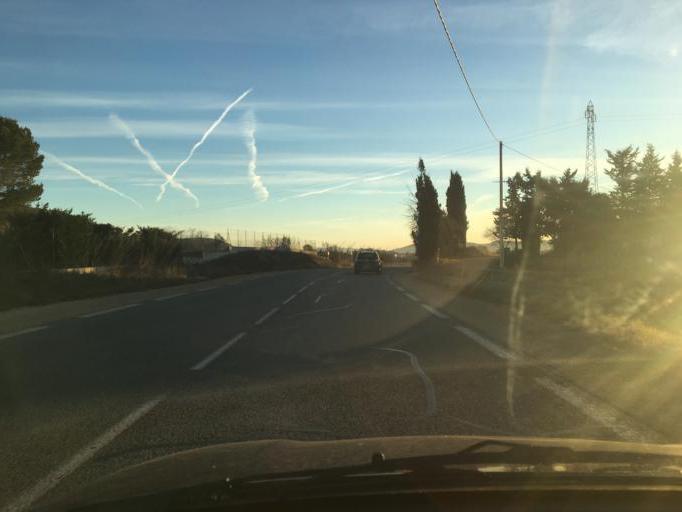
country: FR
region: Provence-Alpes-Cote d'Azur
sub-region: Departement du Var
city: Taradeau
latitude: 43.4496
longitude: 6.4438
